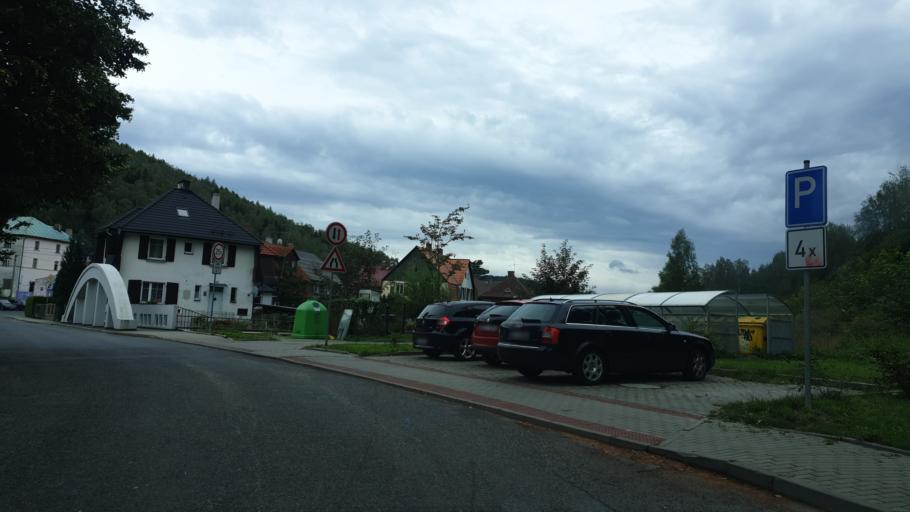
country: CZ
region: Karlovarsky
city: Kraslice
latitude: 50.3215
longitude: 12.5159
